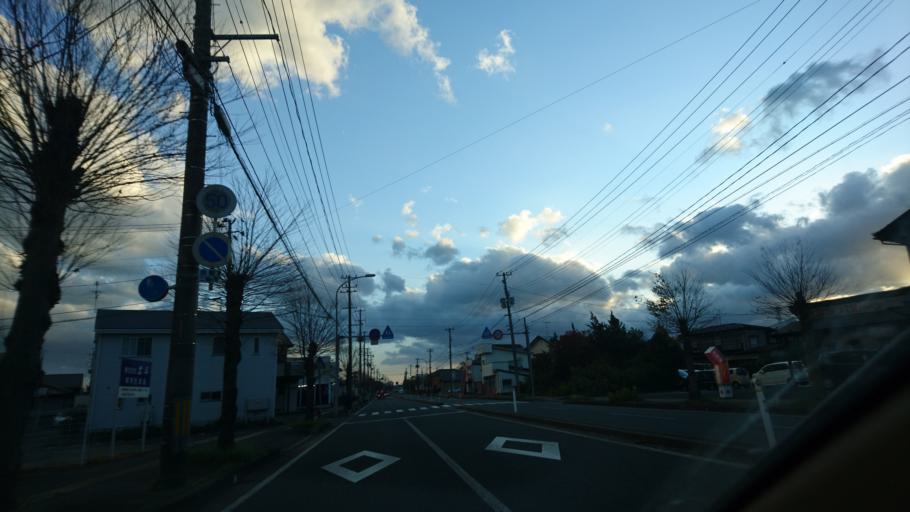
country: JP
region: Iwate
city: Mizusawa
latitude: 39.1502
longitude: 141.1325
